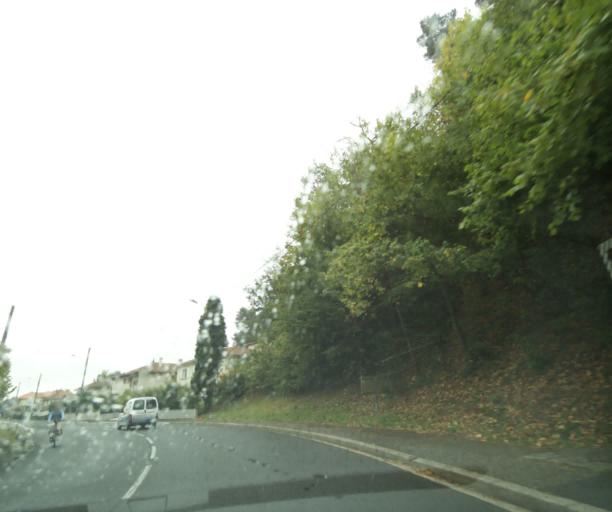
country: FR
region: Auvergne
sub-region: Departement du Puy-de-Dome
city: Ceyrat
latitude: 45.7247
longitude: 3.0638
